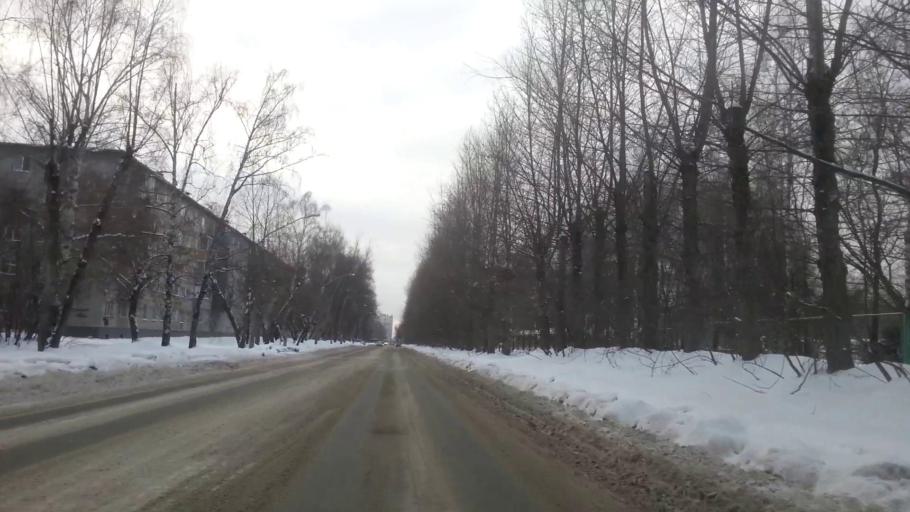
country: RU
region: Altai Krai
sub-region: Gorod Barnaulskiy
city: Barnaul
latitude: 53.3685
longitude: 83.6936
